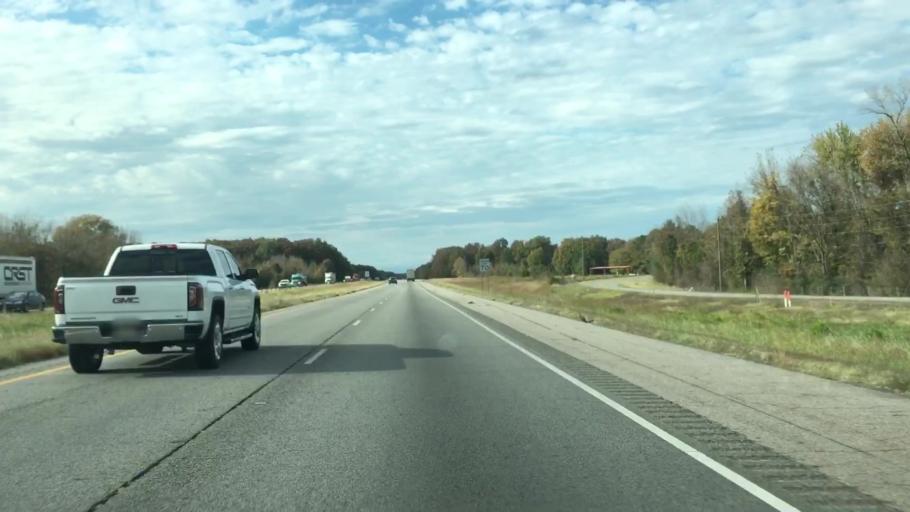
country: US
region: Arkansas
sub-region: Pope County
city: Atkins
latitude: 35.2262
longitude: -92.8390
